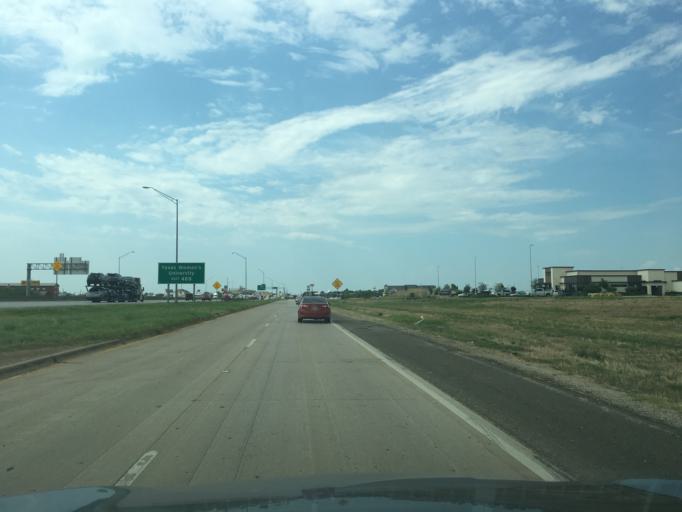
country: US
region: Texas
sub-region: Denton County
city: Denton
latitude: 33.2236
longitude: -97.1716
